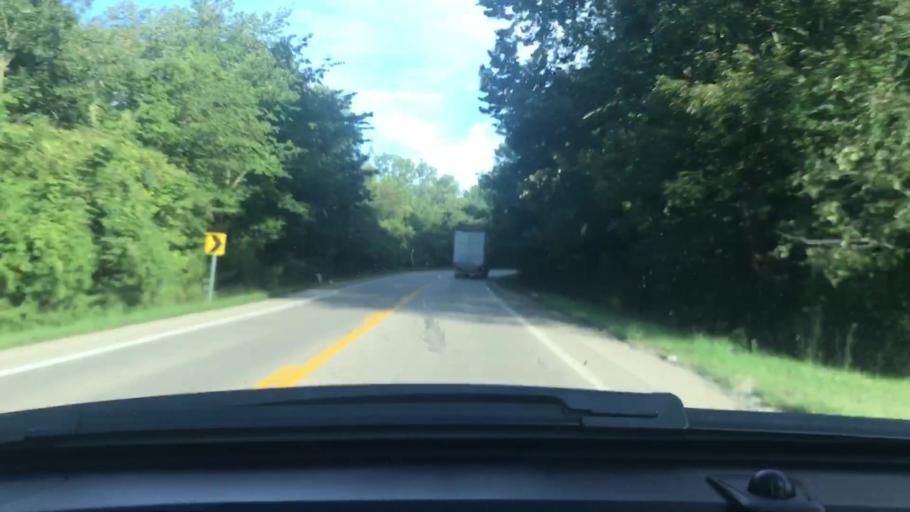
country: US
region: Arkansas
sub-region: Randolph County
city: Pocahontas
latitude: 36.2171
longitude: -91.2174
